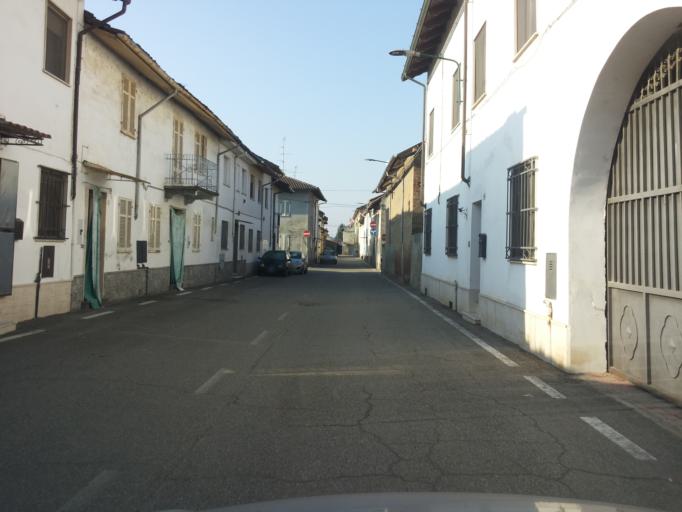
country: IT
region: Piedmont
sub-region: Provincia di Vercelli
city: Caresana
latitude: 45.2224
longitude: 8.5059
